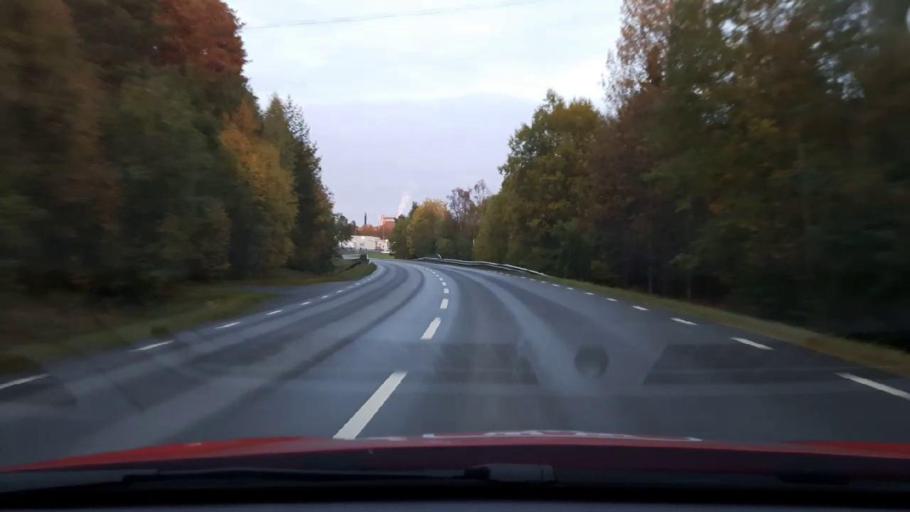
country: SE
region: Jaemtland
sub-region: OEstersunds Kommun
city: Ostersund
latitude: 63.2106
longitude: 14.6283
